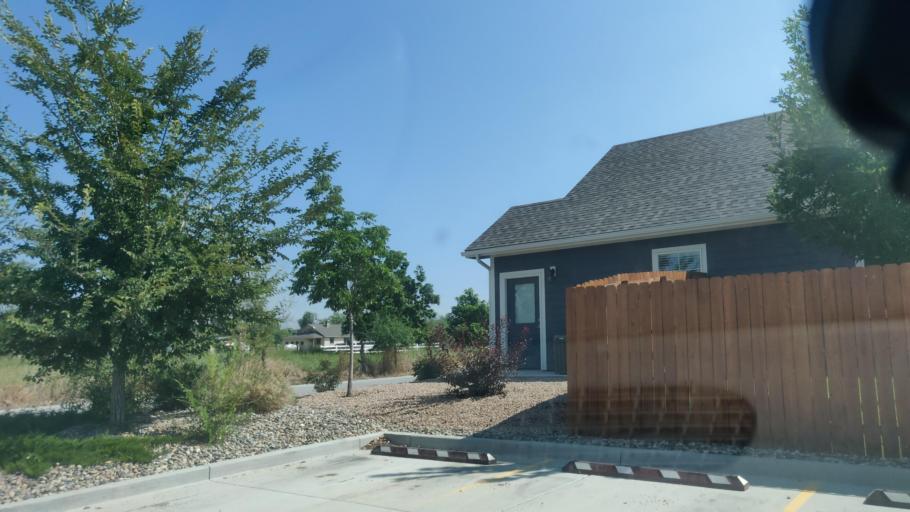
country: US
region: Colorado
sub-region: Mesa County
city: Redlands
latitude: 39.1049
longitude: -108.5908
